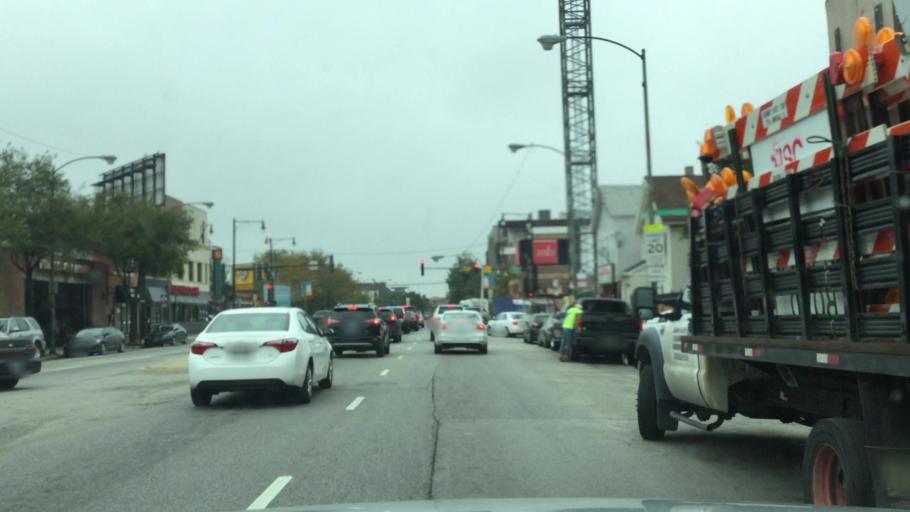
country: US
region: Illinois
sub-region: Cook County
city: Chicago
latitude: 41.9097
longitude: -87.6676
